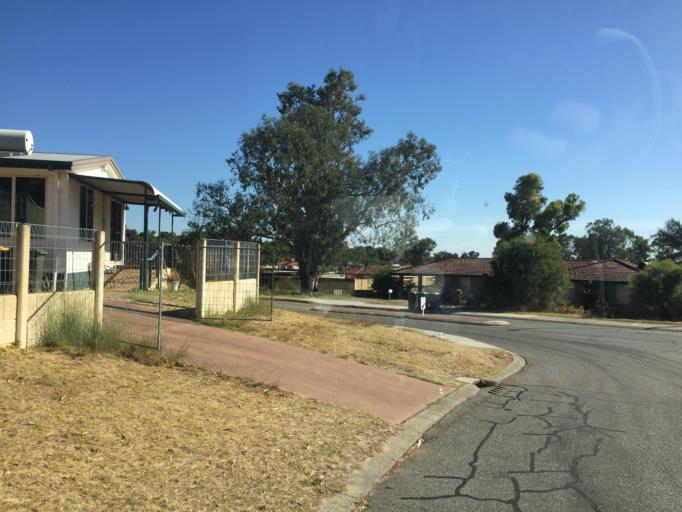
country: AU
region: Western Australia
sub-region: Mundaring
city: Swan View
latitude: -31.8832
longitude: 116.0395
